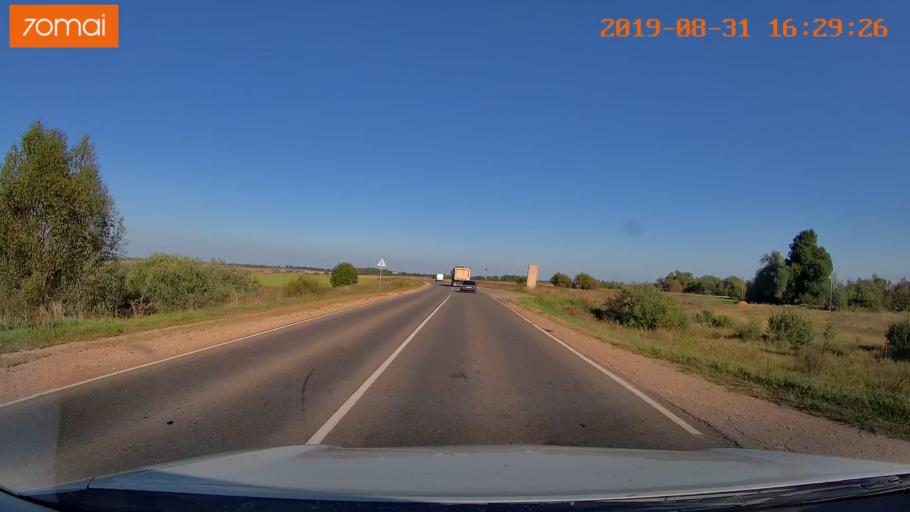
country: RU
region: Kaluga
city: Babynino
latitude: 54.5058
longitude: 35.8054
